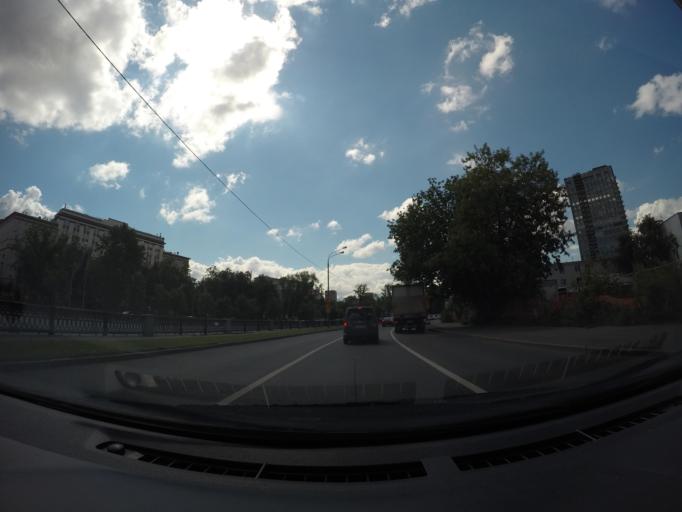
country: RU
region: Moscow
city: Lefortovo
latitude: 55.7784
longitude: 37.7026
